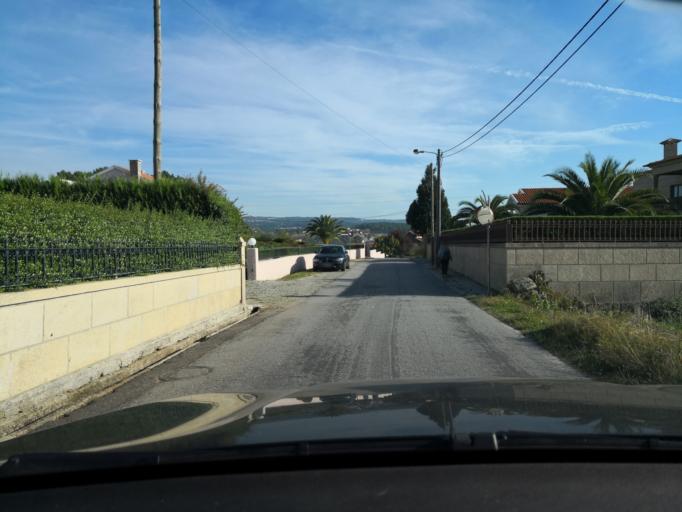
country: PT
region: Vila Real
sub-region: Vila Real
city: Vila Real
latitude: 41.3317
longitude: -7.7423
